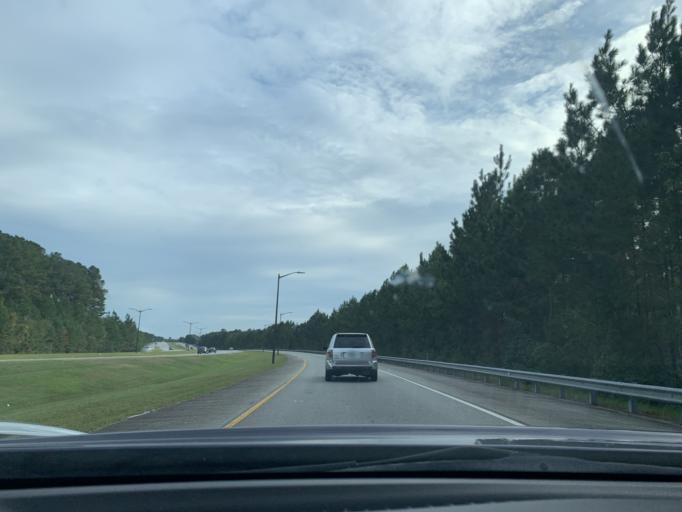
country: US
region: Georgia
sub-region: Chatham County
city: Pooler
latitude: 32.1185
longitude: -81.2697
